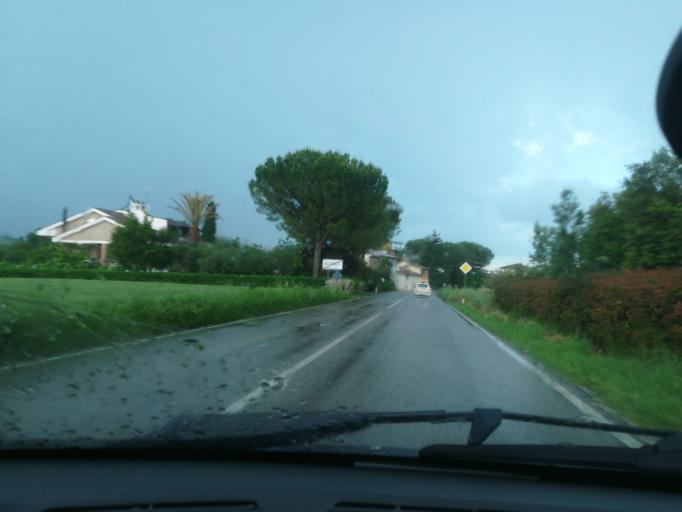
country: IT
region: The Marches
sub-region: Provincia di Macerata
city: Pollenza
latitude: 43.2913
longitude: 13.3629
